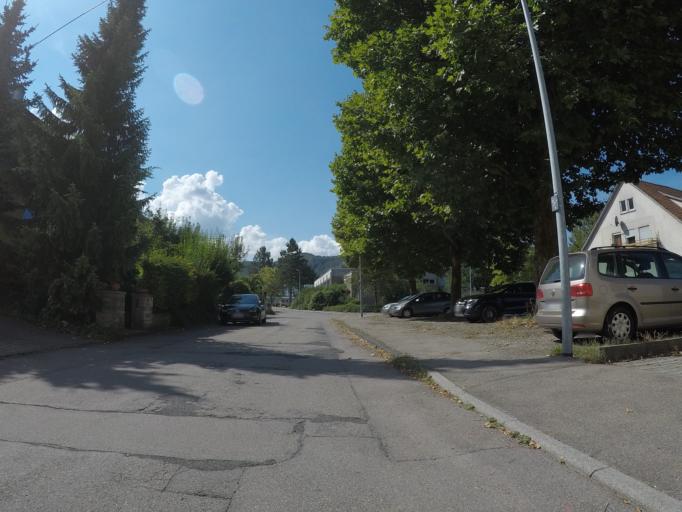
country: DE
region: Baden-Wuerttemberg
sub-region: Tuebingen Region
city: Pfullingen
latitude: 48.4313
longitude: 9.2584
